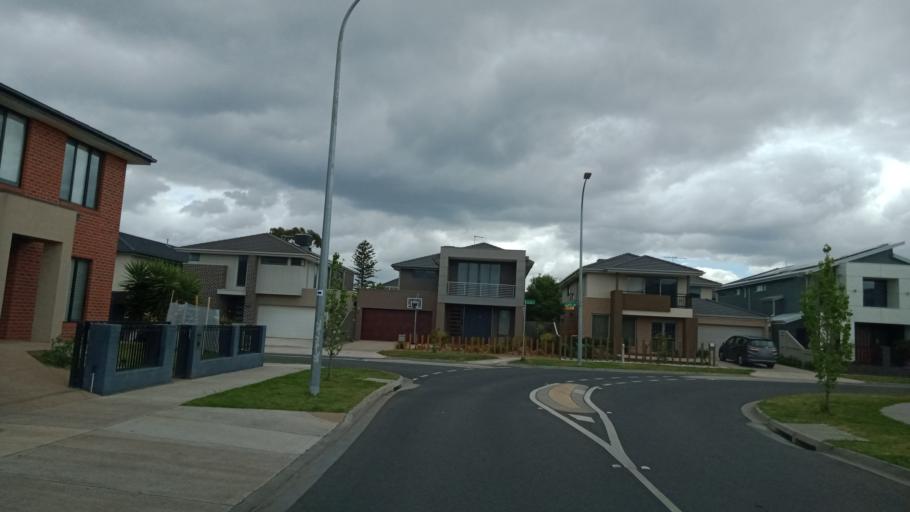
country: AU
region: Victoria
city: McKinnon
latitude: -37.9167
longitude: 145.0552
